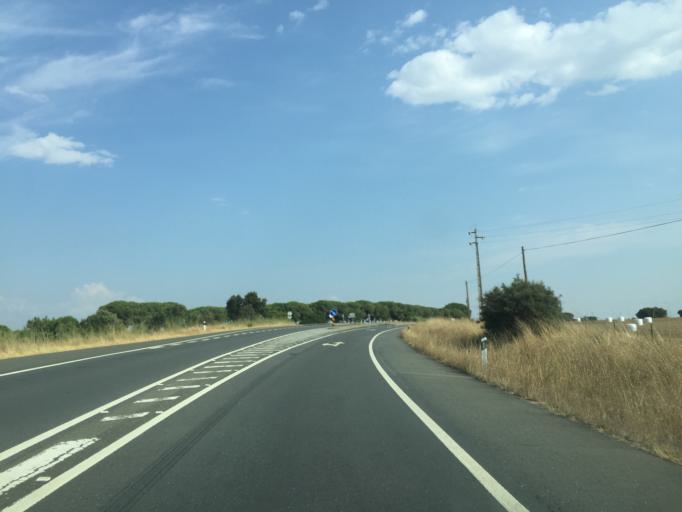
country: PT
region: Setubal
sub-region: Grandola
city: Grandola
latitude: 38.0102
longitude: -8.3798
